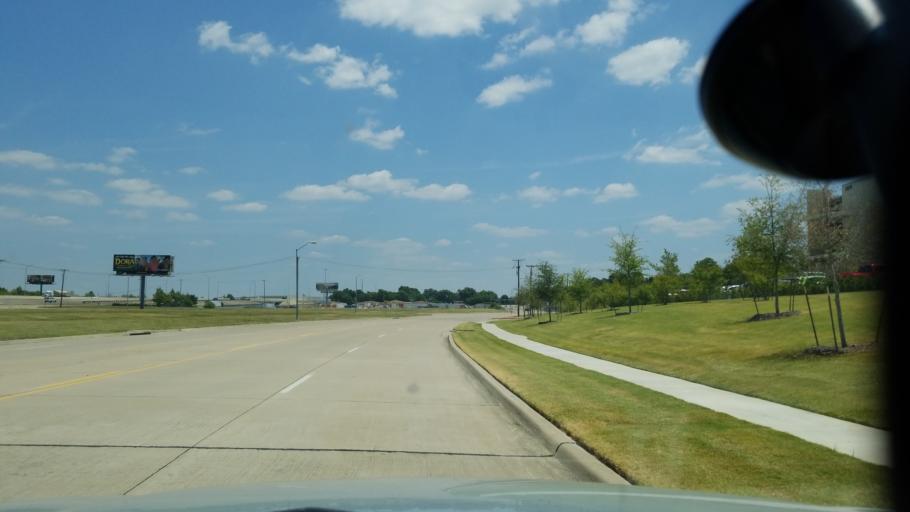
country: US
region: Texas
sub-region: Dallas County
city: Grand Prairie
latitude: 32.7605
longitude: -96.9658
